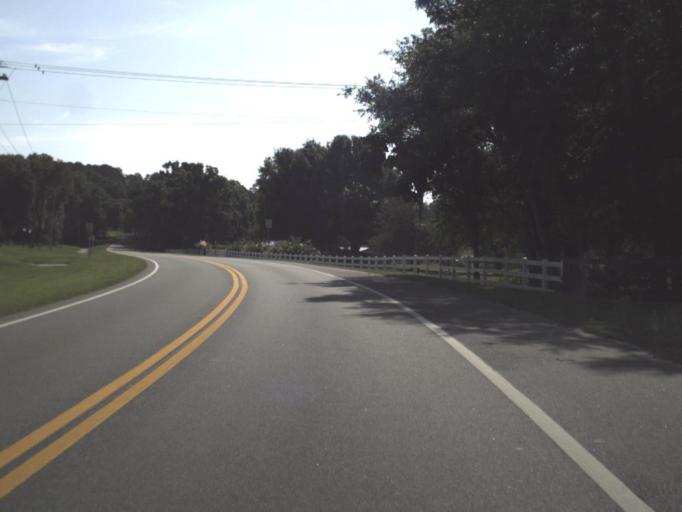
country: US
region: Florida
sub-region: Madison County
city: Madison
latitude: 30.4727
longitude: -83.4045
